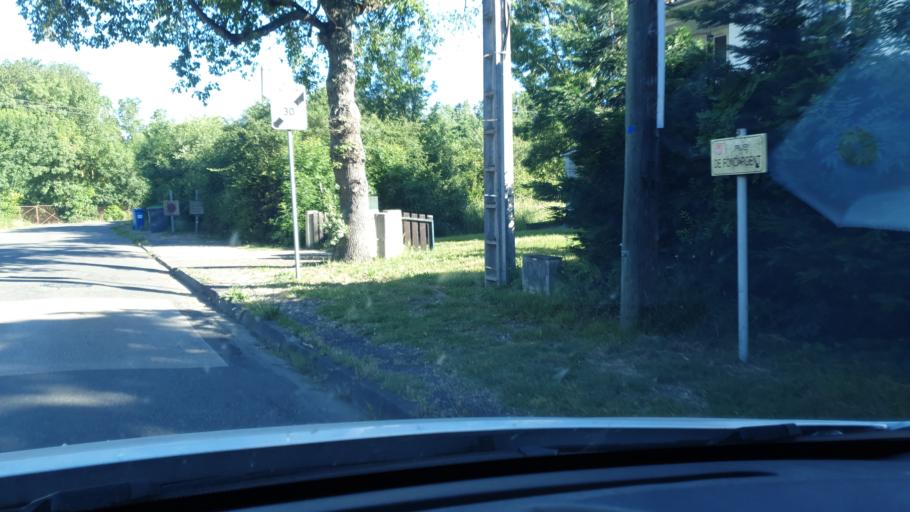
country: FR
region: Midi-Pyrenees
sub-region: Departement de la Haute-Garonne
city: Saint-Orens-de-Gameville
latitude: 43.5602
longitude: 1.5101
